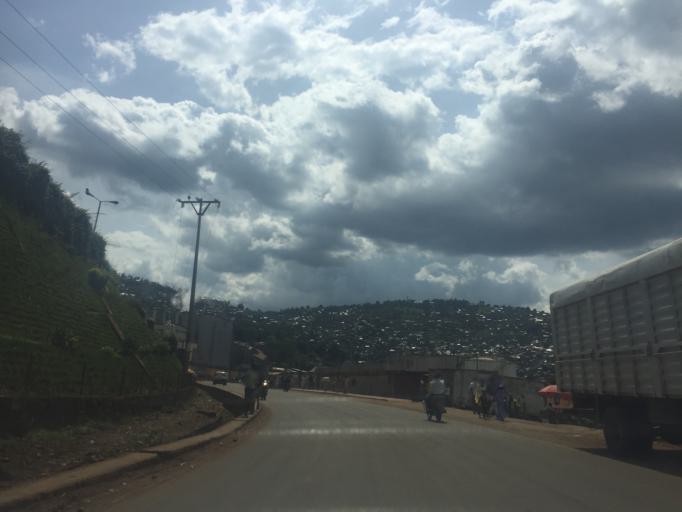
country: CD
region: South Kivu
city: Bukavu
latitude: -2.4839
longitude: 28.8450
